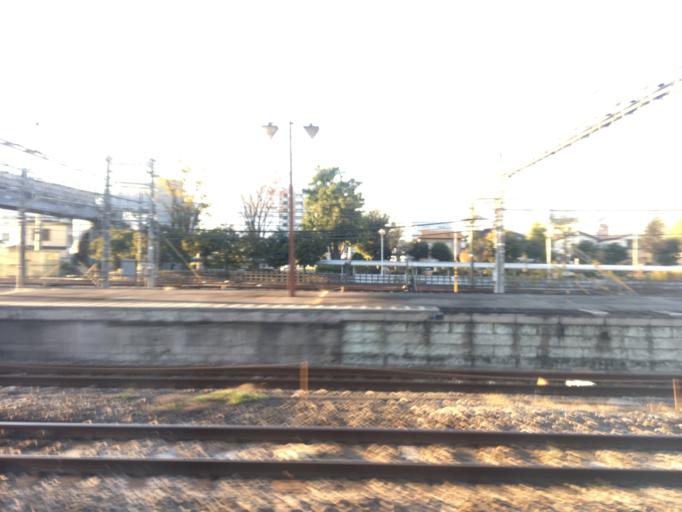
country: JP
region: Gunma
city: Maebashi-shi
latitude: 36.3797
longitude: 139.0479
